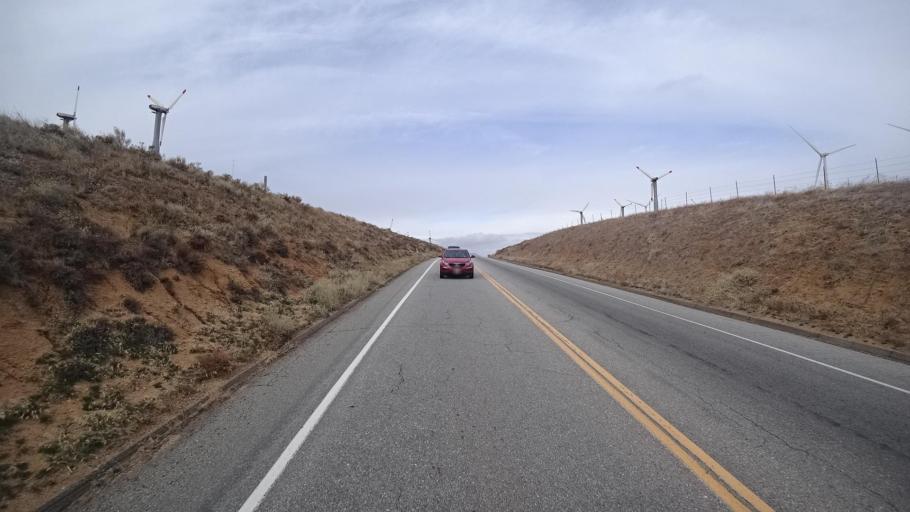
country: US
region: California
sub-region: Kern County
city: Tehachapi
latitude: 35.0604
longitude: -118.3880
